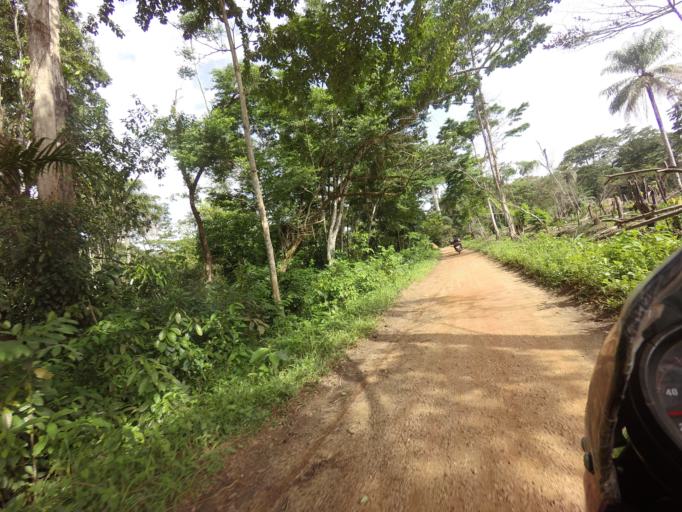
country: SL
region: Eastern Province
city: Jojoima
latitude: 7.8176
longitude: -10.8153
